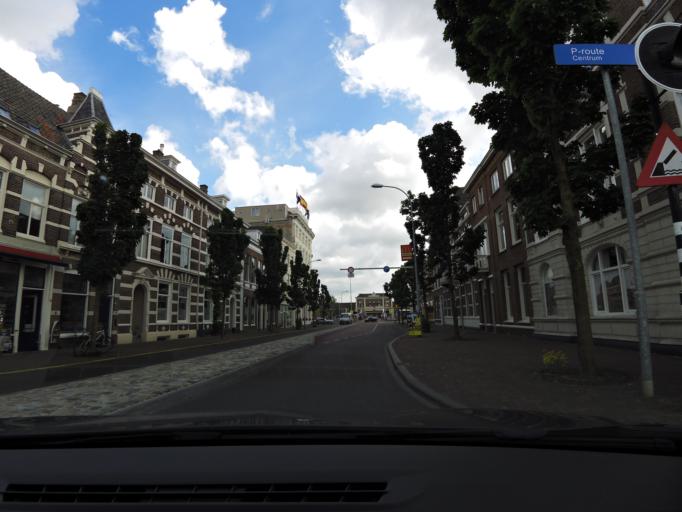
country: NL
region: Zeeland
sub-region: Gemeente Middelburg
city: Middelburg
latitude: 51.4969
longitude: 3.6166
